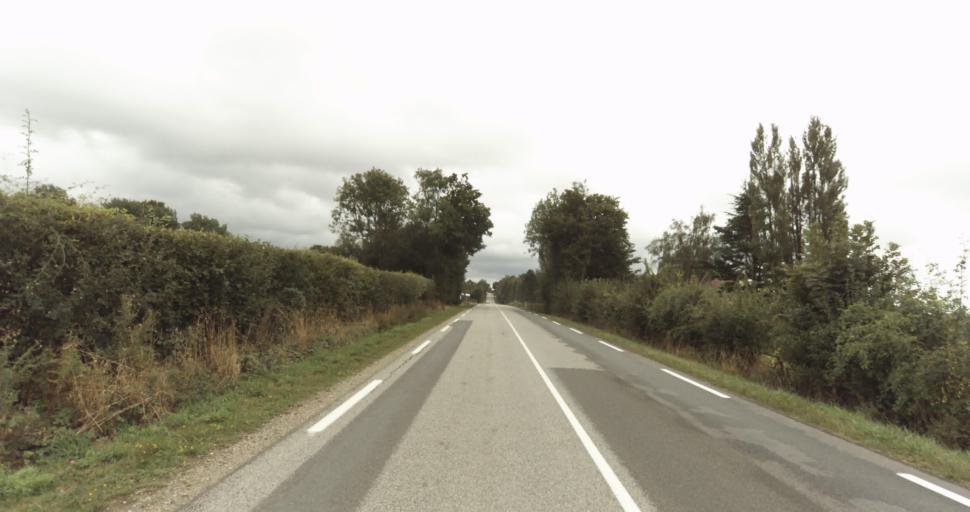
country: FR
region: Lower Normandy
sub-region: Departement de l'Orne
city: Sainte-Gauburge-Sainte-Colombe
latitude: 48.7052
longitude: 0.4371
